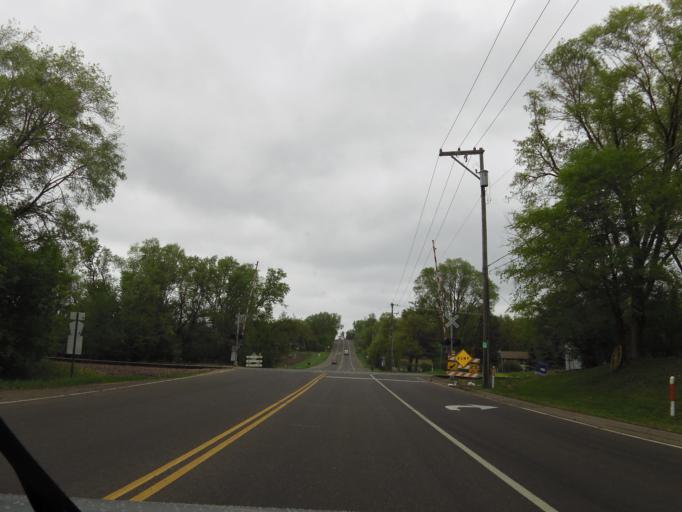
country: US
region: Minnesota
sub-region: Washington County
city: Oak Park Heights
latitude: 45.0153
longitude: -92.8069
